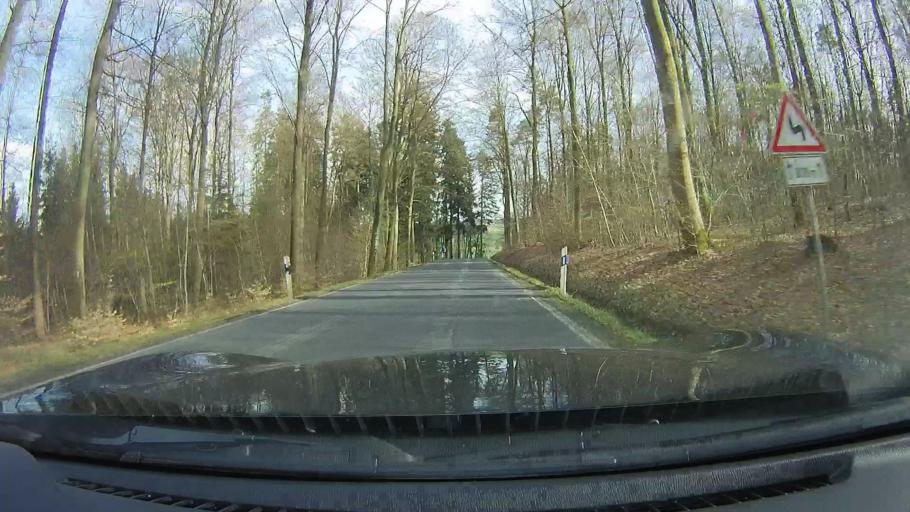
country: DE
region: Bavaria
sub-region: Regierungsbezirk Unterfranken
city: Eichenbuhl
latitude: 49.6484
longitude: 9.3096
